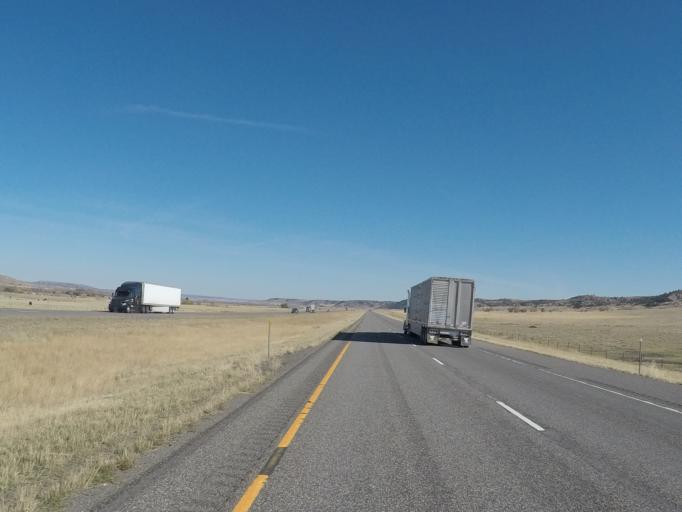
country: US
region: Montana
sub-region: Sweet Grass County
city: Big Timber
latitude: 45.7522
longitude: -110.1523
